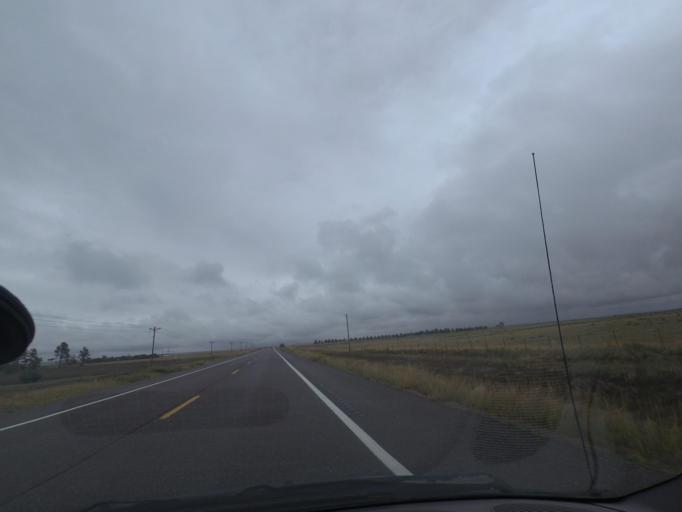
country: US
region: Colorado
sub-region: Arapahoe County
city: Byers
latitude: 39.7397
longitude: -104.1290
